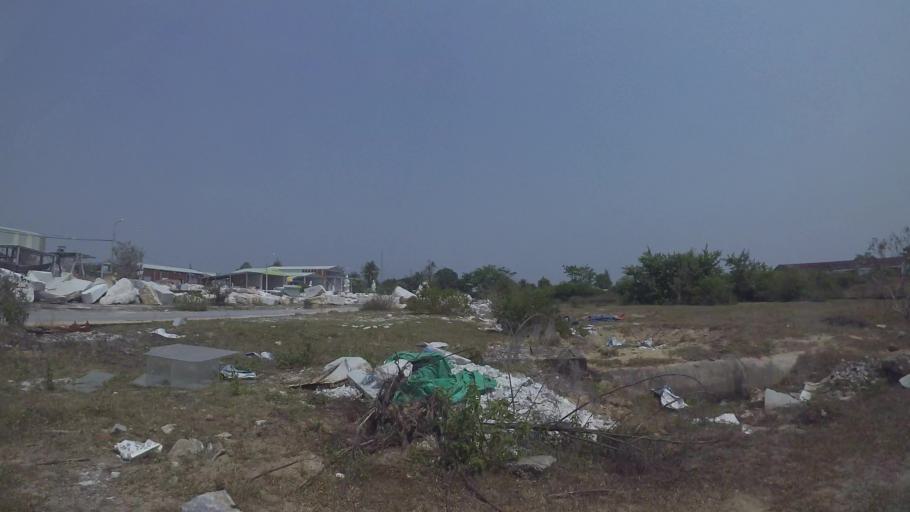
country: VN
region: Da Nang
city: Ngu Hanh Son
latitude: 15.9881
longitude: 108.2519
